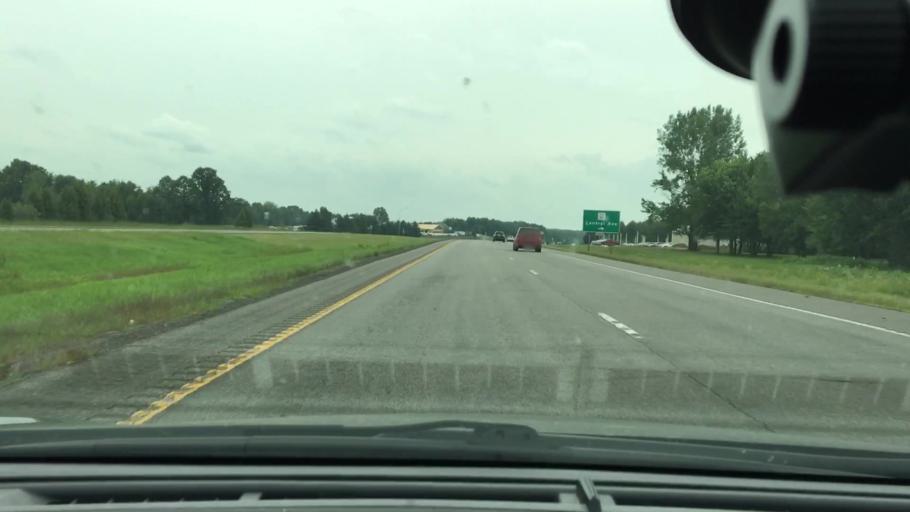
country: US
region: Minnesota
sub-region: Mille Lacs County
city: Milaca
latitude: 45.7875
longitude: -93.6536
